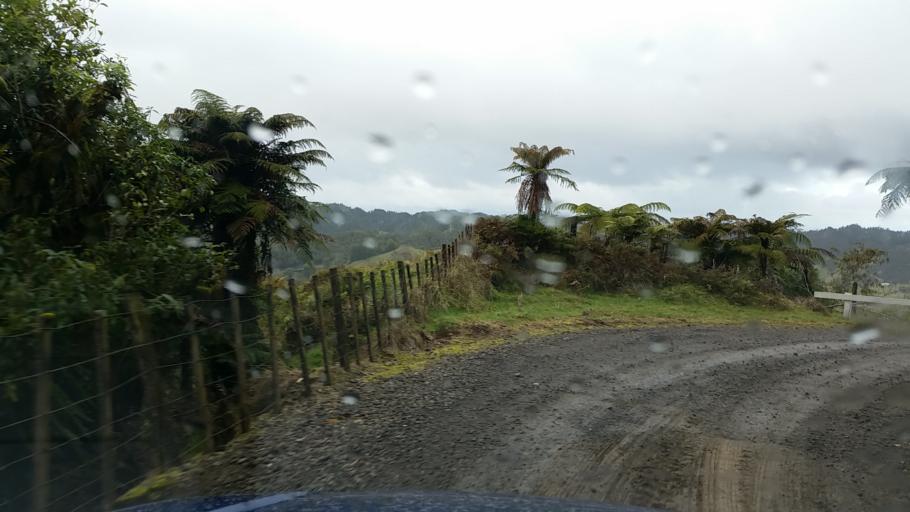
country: NZ
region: Taranaki
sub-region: South Taranaki District
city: Eltham
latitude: -39.1685
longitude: 174.6285
